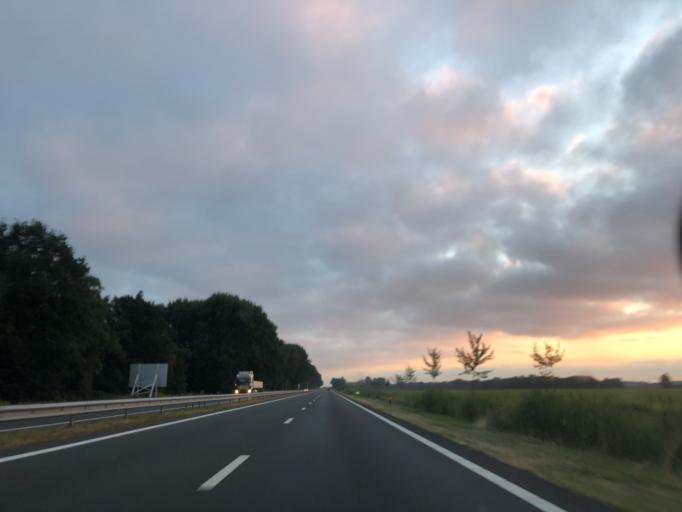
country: NL
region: Groningen
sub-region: Gemeente Veendam
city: Veendam
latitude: 53.1123
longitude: 6.8996
